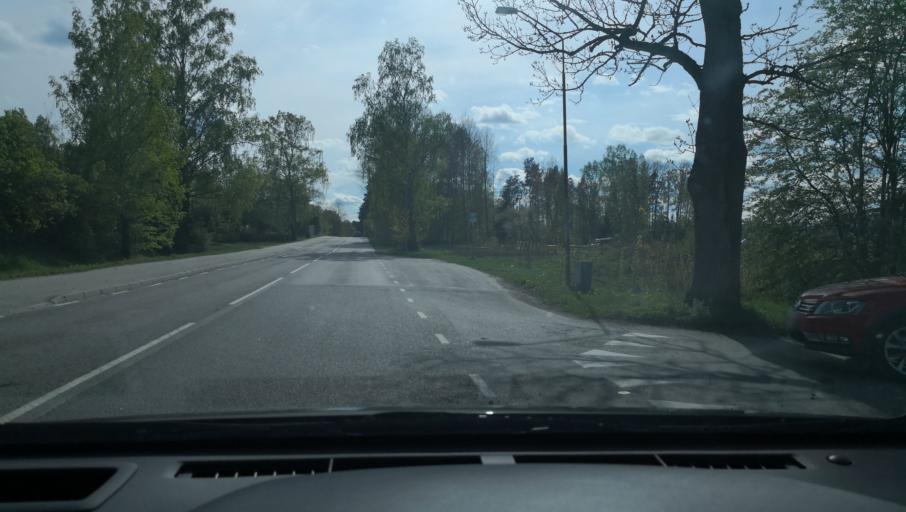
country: SE
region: OErebro
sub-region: Hallsbergs Kommun
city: Hallsberg
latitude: 59.0571
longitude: 15.0591
